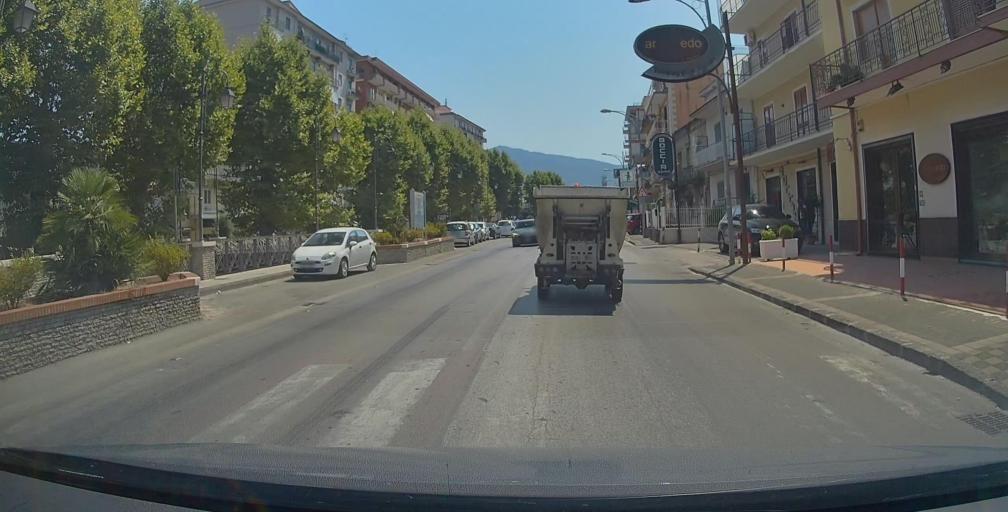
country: IT
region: Campania
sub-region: Provincia di Salerno
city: Nocera Superiore
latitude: 40.7400
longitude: 14.6700
